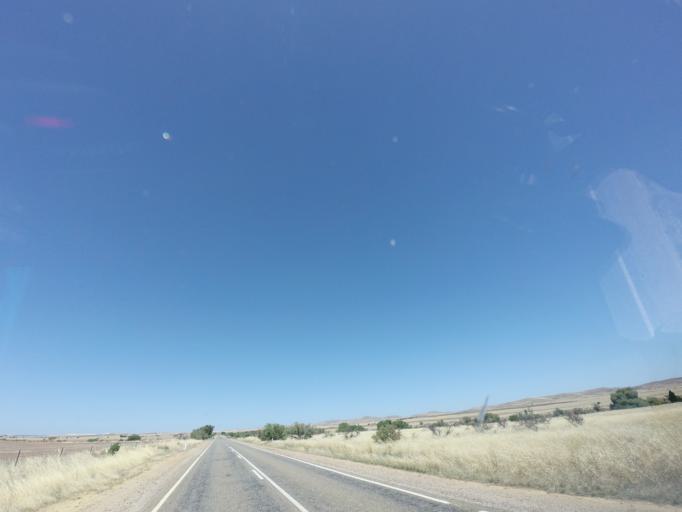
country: AU
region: South Australia
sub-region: Peterborough
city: Peterborough
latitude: -32.7139
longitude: 138.4557
